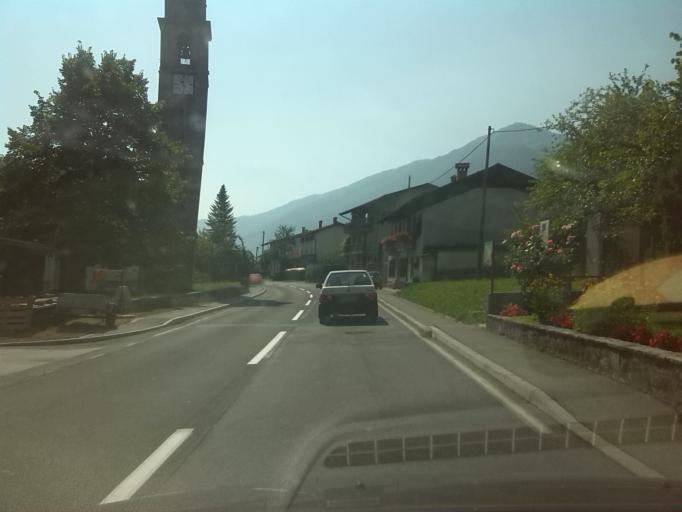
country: SI
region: Kobarid
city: Kobarid
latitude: 46.2331
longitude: 13.5907
